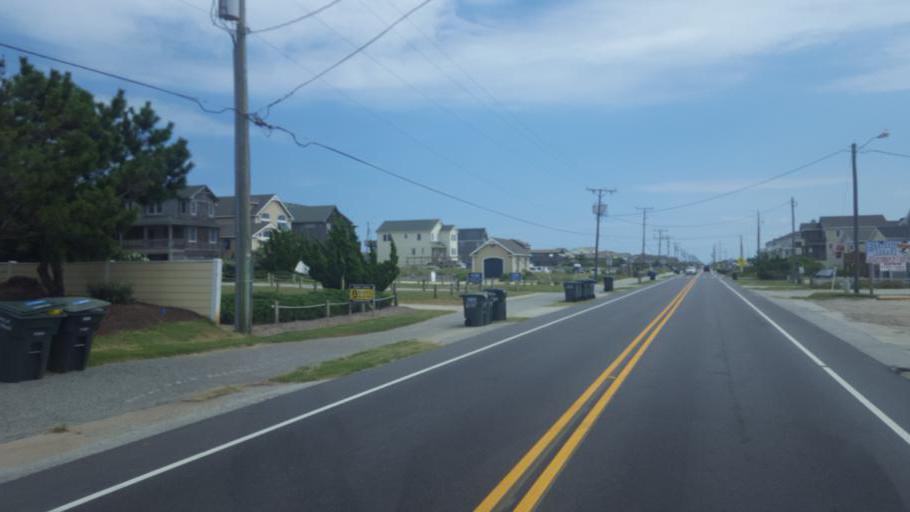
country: US
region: North Carolina
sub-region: Dare County
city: Nags Head
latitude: 35.9687
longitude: -75.6306
